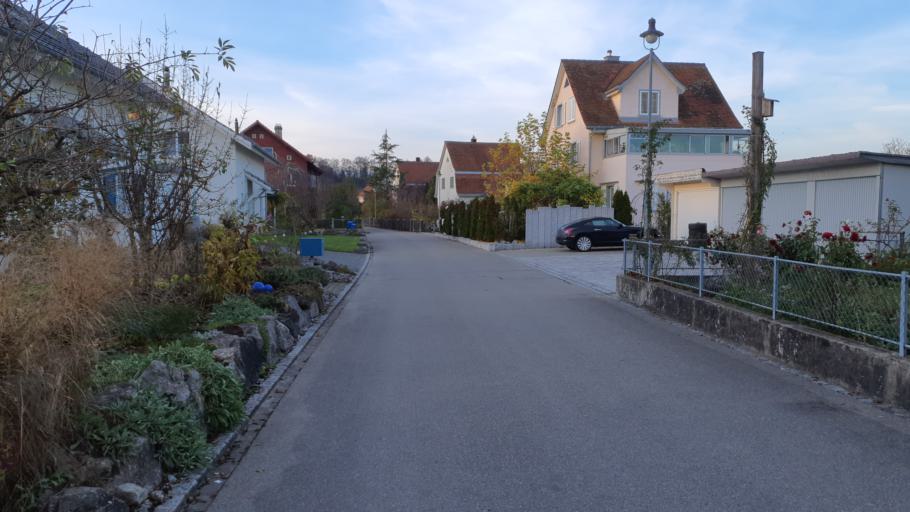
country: CH
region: Zurich
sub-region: Bezirk Andelfingen
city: Dachsen
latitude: 47.6462
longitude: 8.6055
